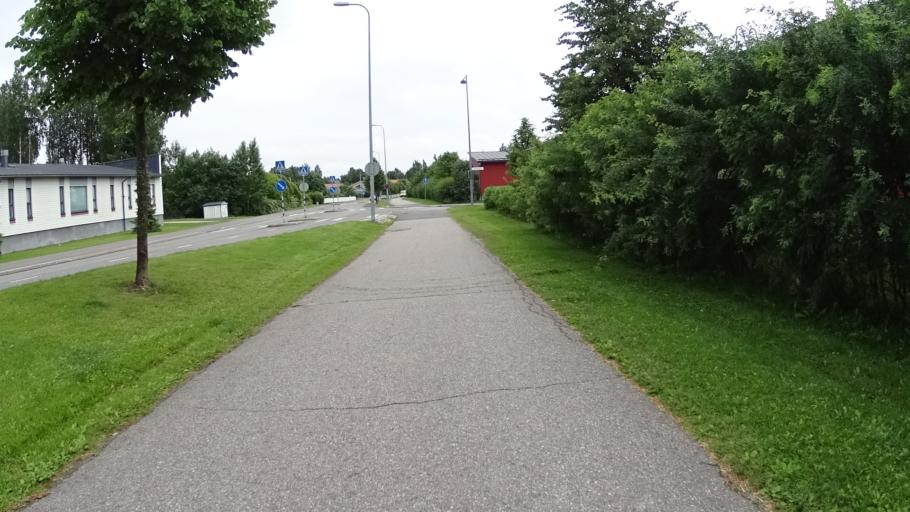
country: FI
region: Uusimaa
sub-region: Helsinki
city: Helsinki
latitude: 60.2783
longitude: 24.9100
